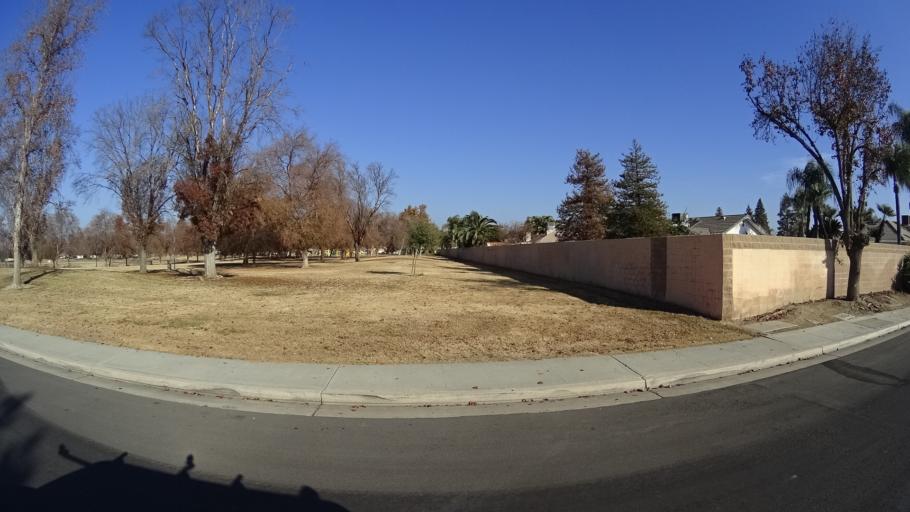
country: US
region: California
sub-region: Kern County
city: Greenacres
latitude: 35.3198
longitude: -119.1061
